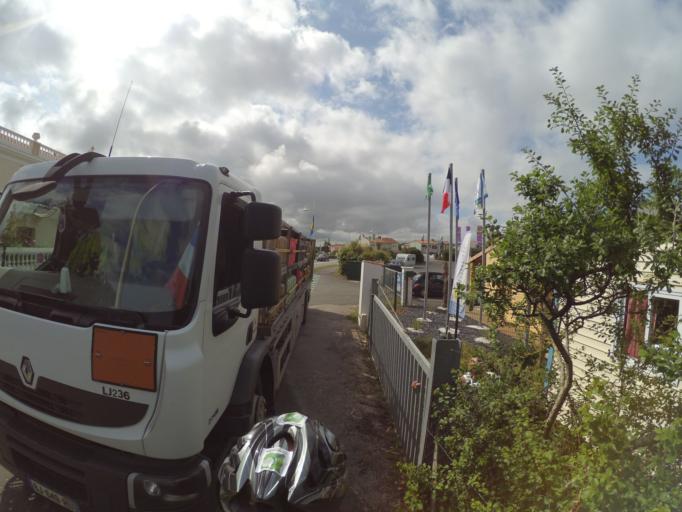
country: FR
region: Poitou-Charentes
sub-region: Departement de la Charente-Maritime
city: Chatelaillon-Plage
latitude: 46.0846
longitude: -1.0934
